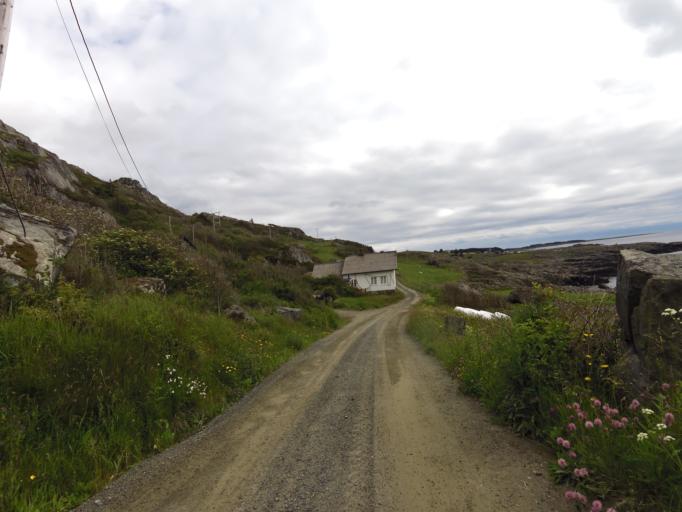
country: NO
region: Vest-Agder
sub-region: Farsund
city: Vestbygd
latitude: 58.1473
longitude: 6.6141
